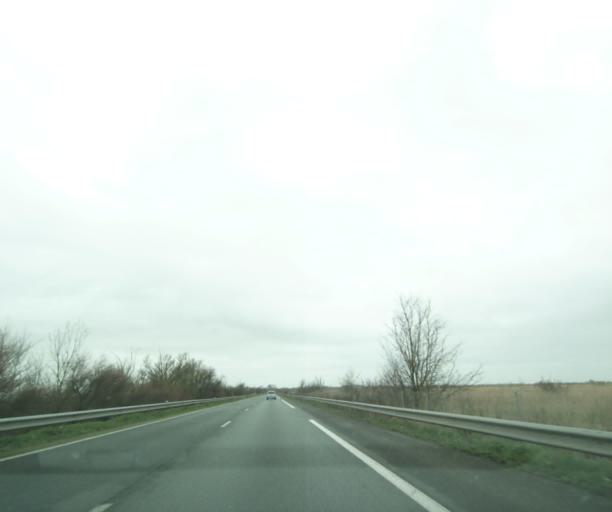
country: FR
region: Poitou-Charentes
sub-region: Departement de la Charente-Maritime
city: Breuil-Magne
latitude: 45.9756
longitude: -0.9917
